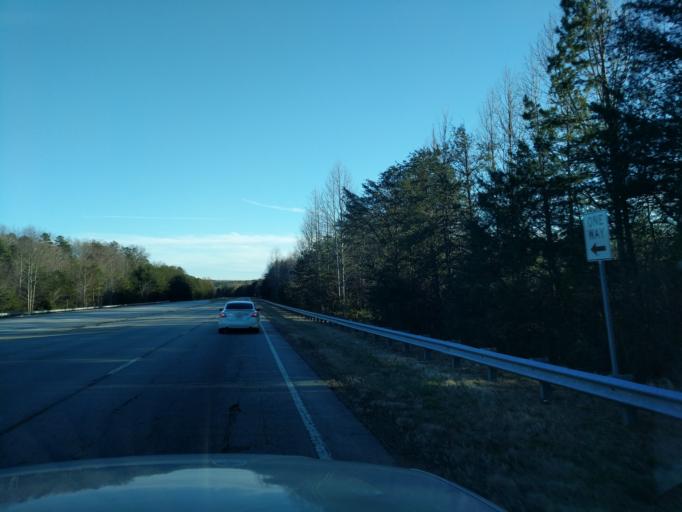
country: US
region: Georgia
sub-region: Stephens County
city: Toccoa
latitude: 34.5716
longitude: -83.4023
